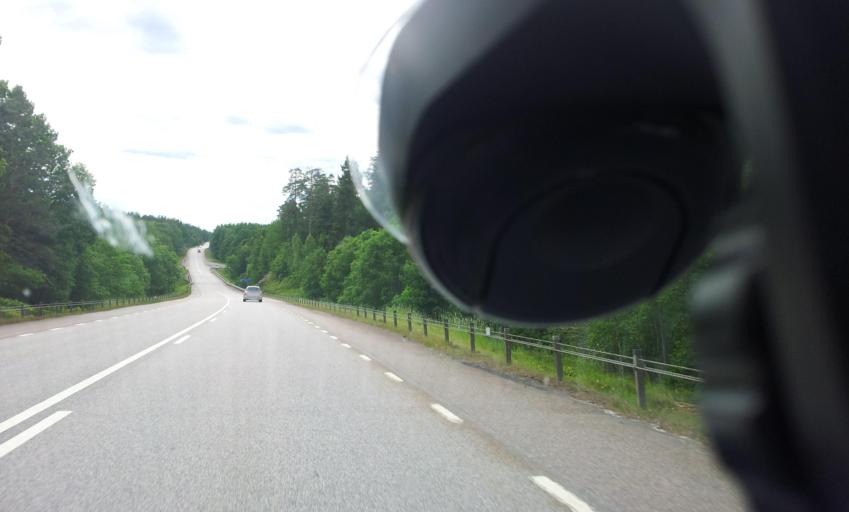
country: SE
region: Kalmar
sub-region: Vasterviks Kommun
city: Ankarsrum
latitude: 57.5532
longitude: 16.4752
